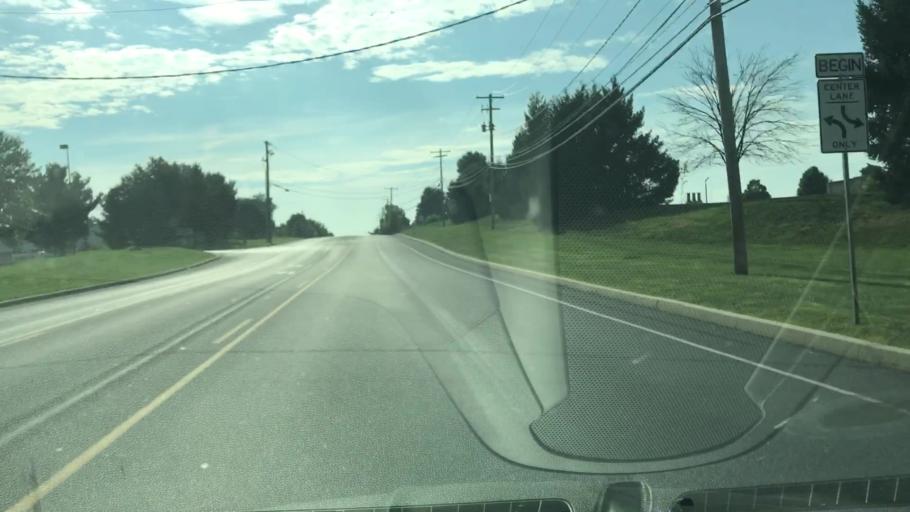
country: US
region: Pennsylvania
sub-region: Dauphin County
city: Middletown
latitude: 40.2300
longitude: -76.7418
